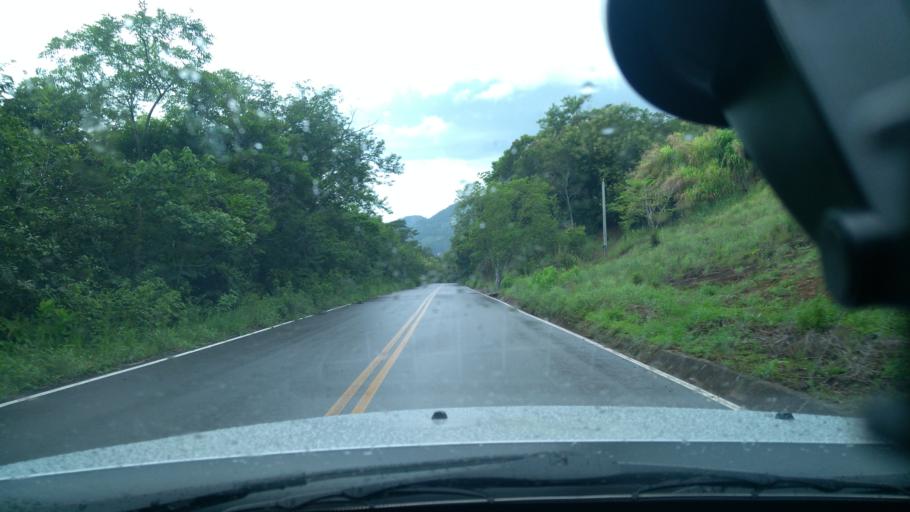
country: BR
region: Rio Grande do Sul
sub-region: Torres
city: Torres
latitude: -29.1948
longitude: -49.9745
